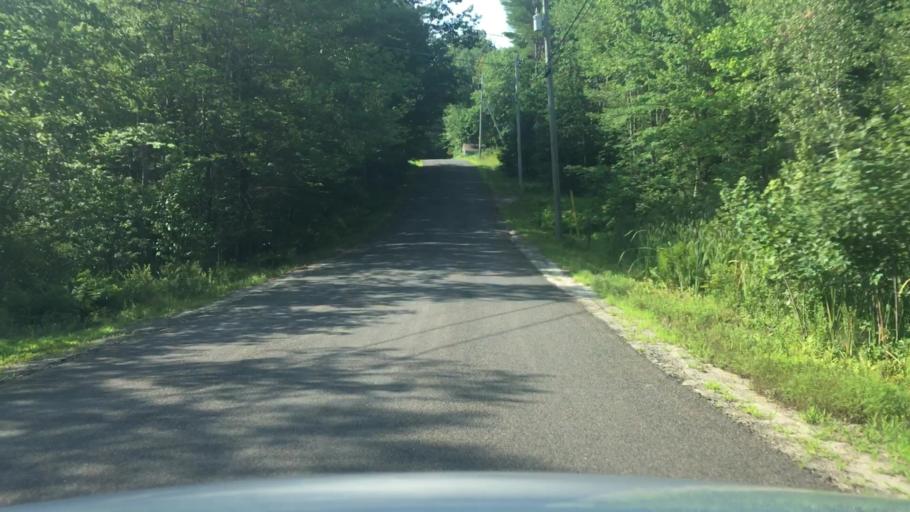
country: US
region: Maine
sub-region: Androscoggin County
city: Greene
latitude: 44.2389
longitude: -70.1058
